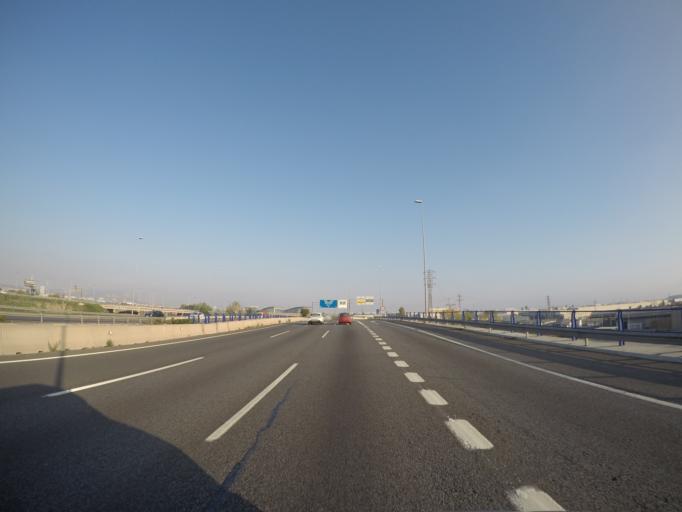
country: ES
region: Catalonia
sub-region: Provincia de Barcelona
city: El Prat de Llobregat
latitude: 41.3397
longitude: 2.1147
